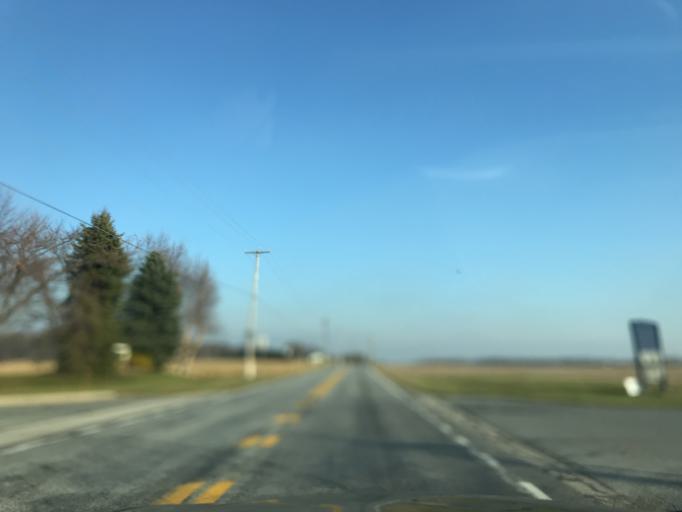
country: US
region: Pennsylvania
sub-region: York County
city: New Freedom
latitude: 39.7393
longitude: -76.6882
